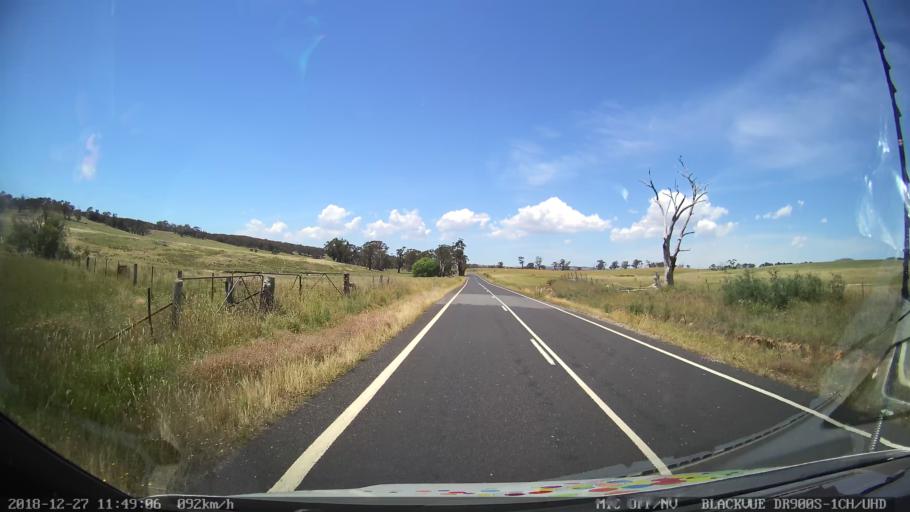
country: AU
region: New South Wales
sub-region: Bathurst Regional
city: Perthville
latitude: -33.6144
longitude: 149.4352
